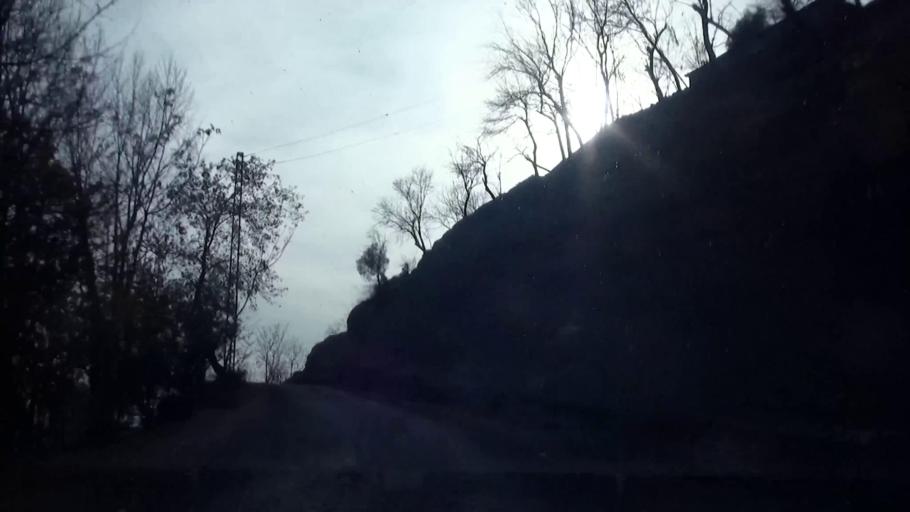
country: PK
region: Azad Kashmir
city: Muzaffarabad
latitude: 34.3659
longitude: 73.5271
